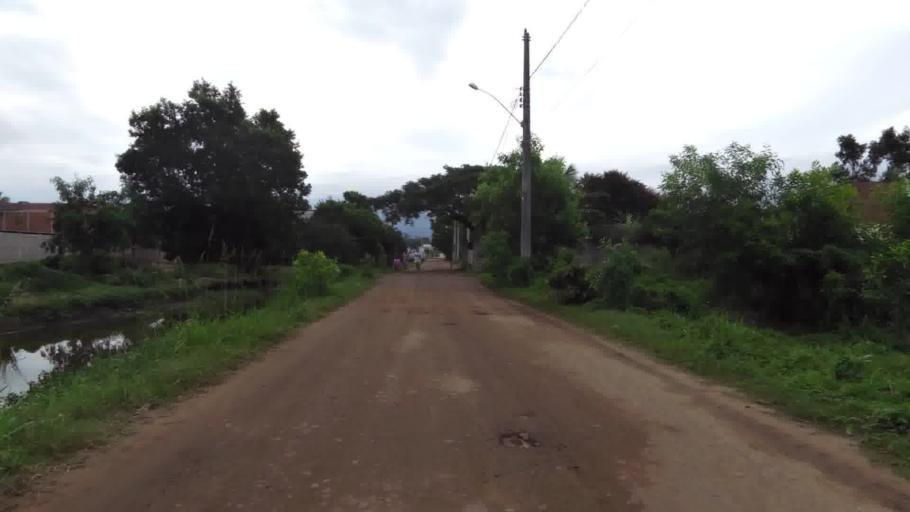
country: BR
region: Espirito Santo
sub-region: Piuma
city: Piuma
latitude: -20.8060
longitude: -40.6391
